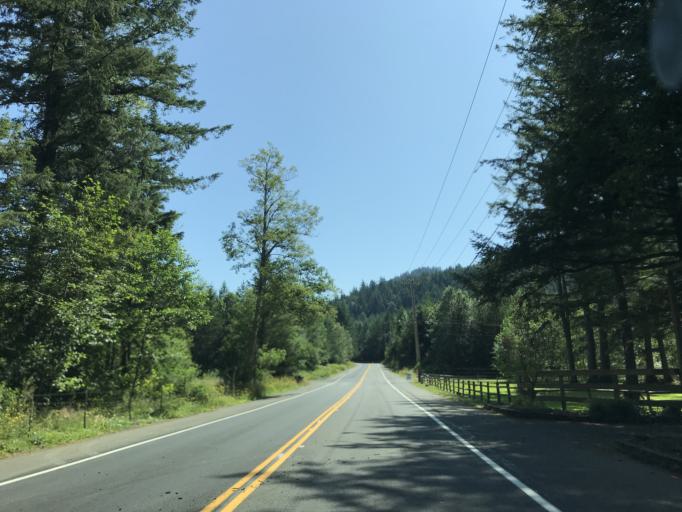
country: US
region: Washington
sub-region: King County
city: Ravensdale
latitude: 47.3564
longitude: -121.8919
